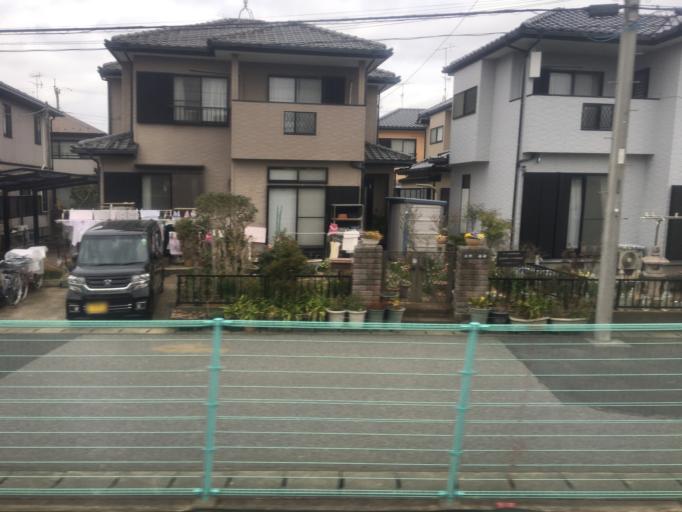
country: JP
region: Chiba
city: Togane
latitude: 35.5640
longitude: 140.3712
